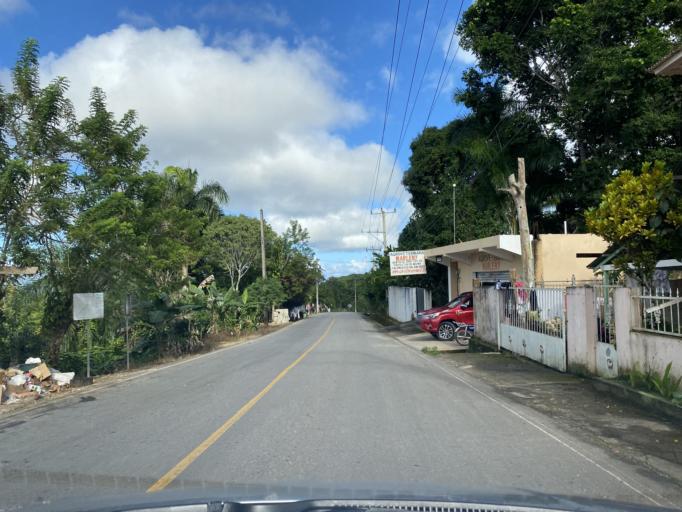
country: DO
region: Samana
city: Las Terrenas
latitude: 19.2722
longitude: -69.5534
